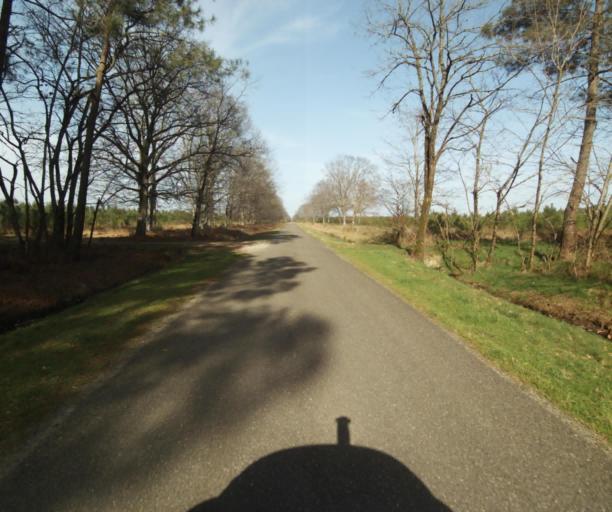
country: FR
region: Aquitaine
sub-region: Departement des Landes
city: Roquefort
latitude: 44.1615
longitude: -0.1669
